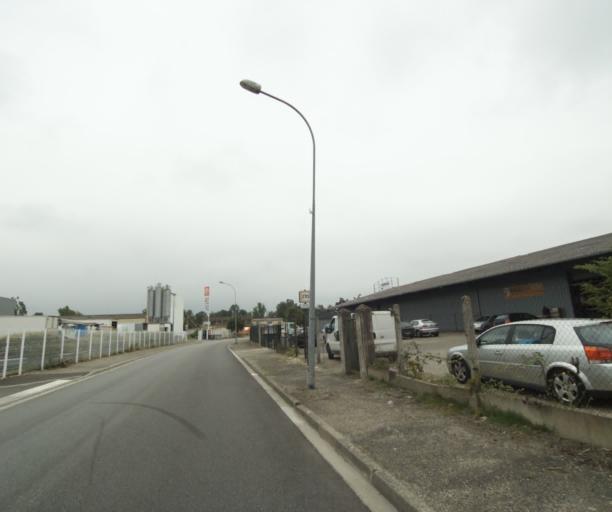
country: FR
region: Midi-Pyrenees
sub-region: Departement du Tarn-et-Garonne
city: Bressols
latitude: 43.9787
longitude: 1.3313
